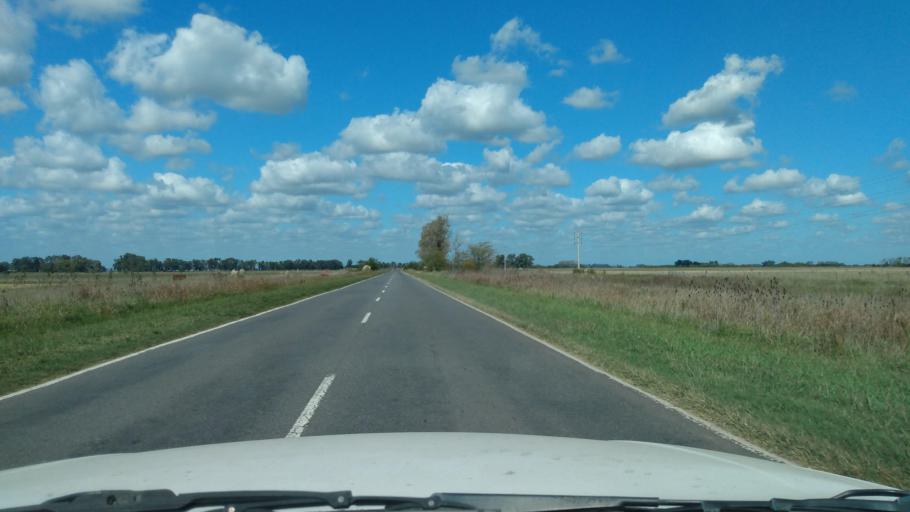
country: AR
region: Buenos Aires
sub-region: Partido de Navarro
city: Navarro
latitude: -34.8680
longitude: -59.3424
